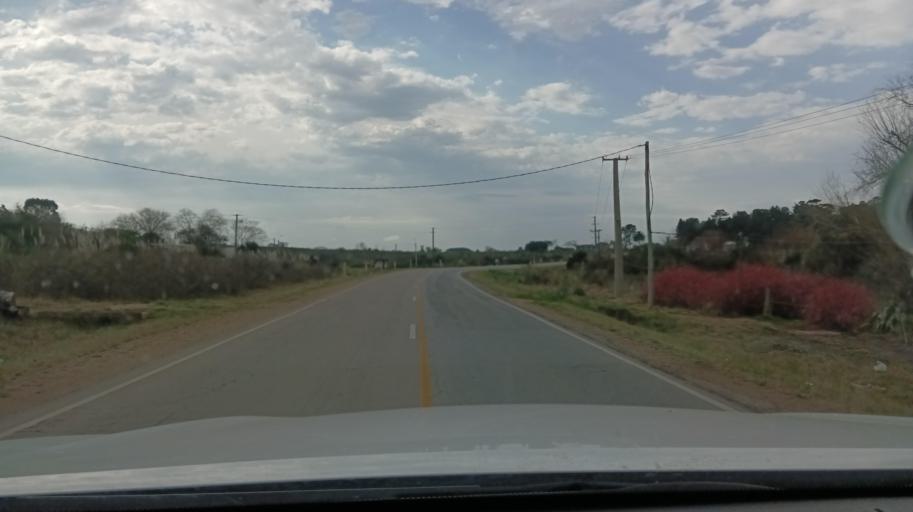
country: UY
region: Canelones
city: Toledo
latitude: -34.7119
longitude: -56.1112
